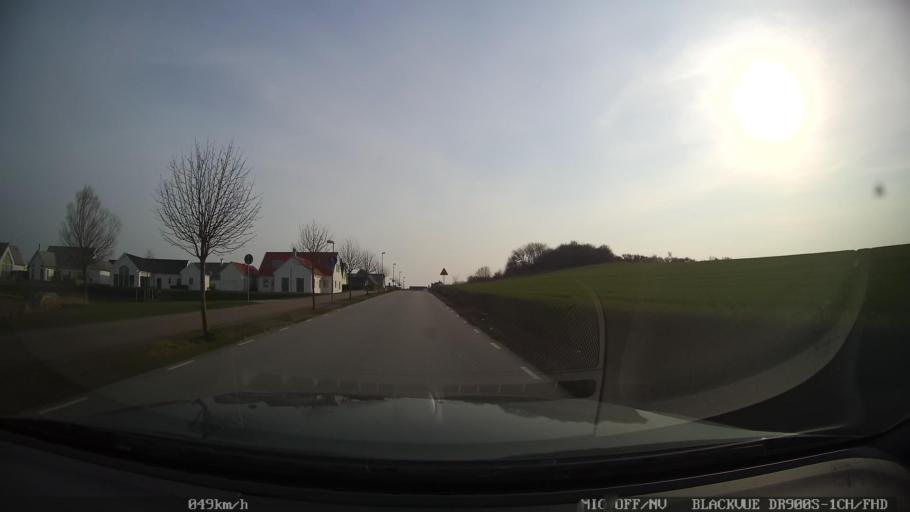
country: SE
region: Skane
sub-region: Ystads Kommun
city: Ystad
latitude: 55.4472
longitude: 13.7952
